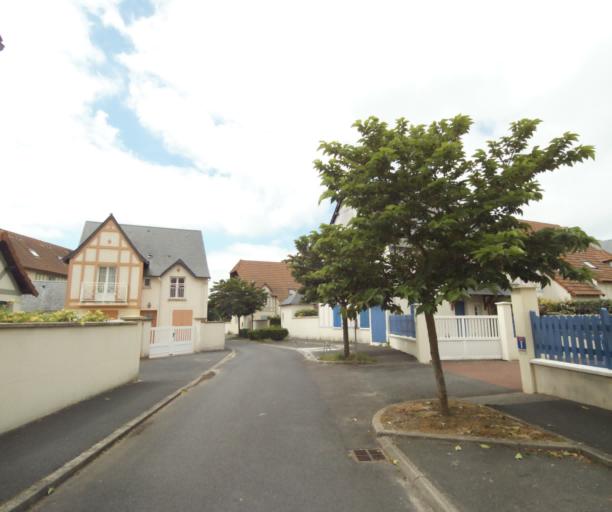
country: FR
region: Lower Normandy
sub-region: Departement du Calvados
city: Dives-sur-Mer
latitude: 49.2949
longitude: -0.0968
